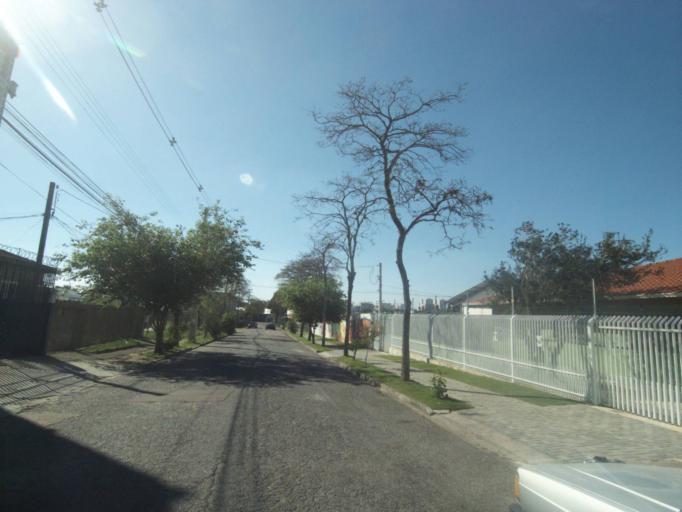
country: BR
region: Parana
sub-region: Curitiba
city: Curitiba
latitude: -25.3969
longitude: -49.2340
